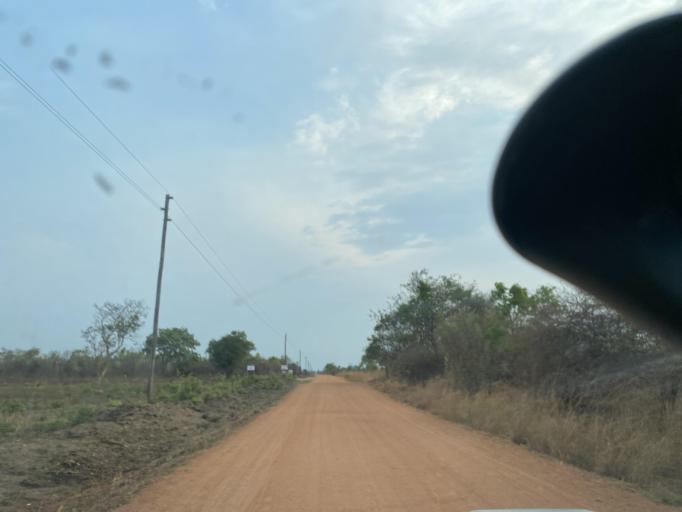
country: ZM
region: Lusaka
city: Chongwe
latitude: -15.2004
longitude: 28.5812
